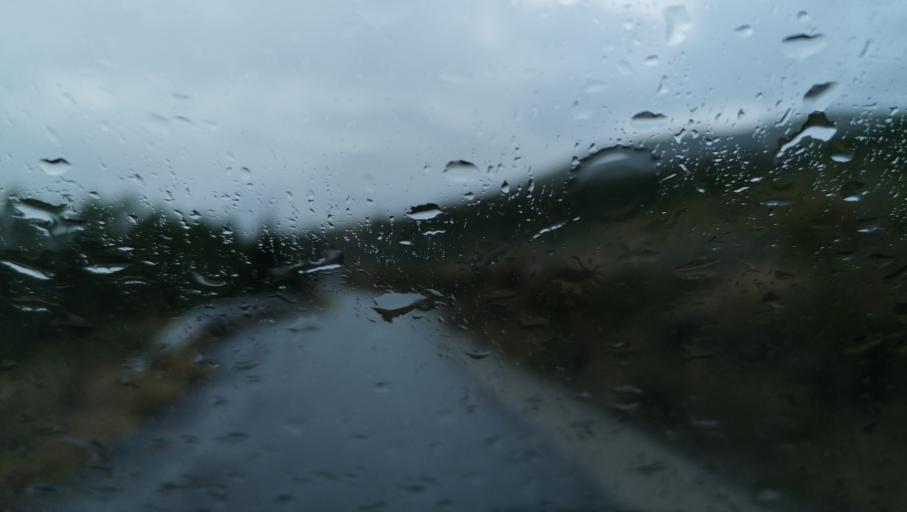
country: PT
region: Vila Real
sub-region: Vila Pouca de Aguiar
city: Vila Pouca de Aguiar
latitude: 41.5538
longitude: -7.7109
